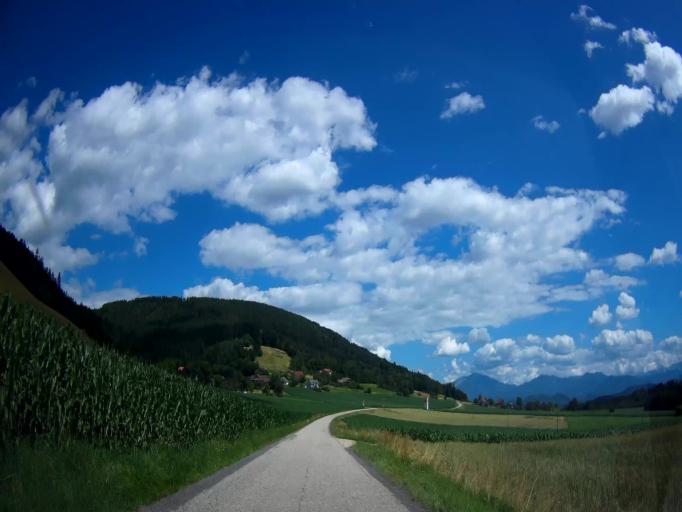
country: AT
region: Carinthia
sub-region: Politischer Bezirk Klagenfurt Land
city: Poggersdorf
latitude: 46.6728
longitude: 14.5250
